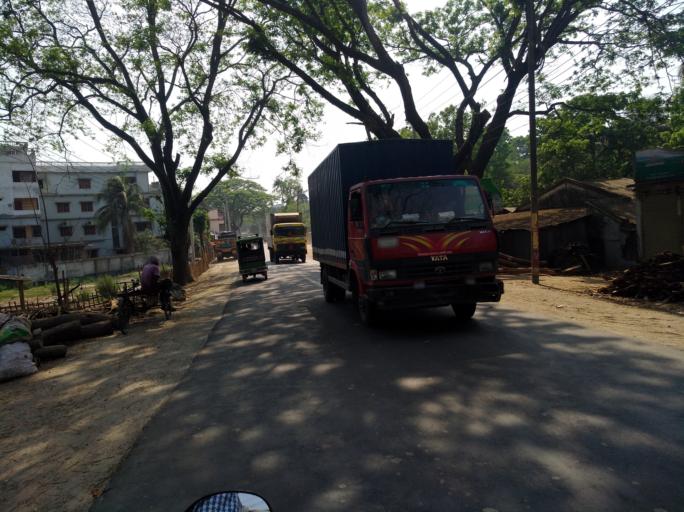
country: BD
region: Khulna
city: Kaliganj
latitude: 23.5490
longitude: 89.1679
